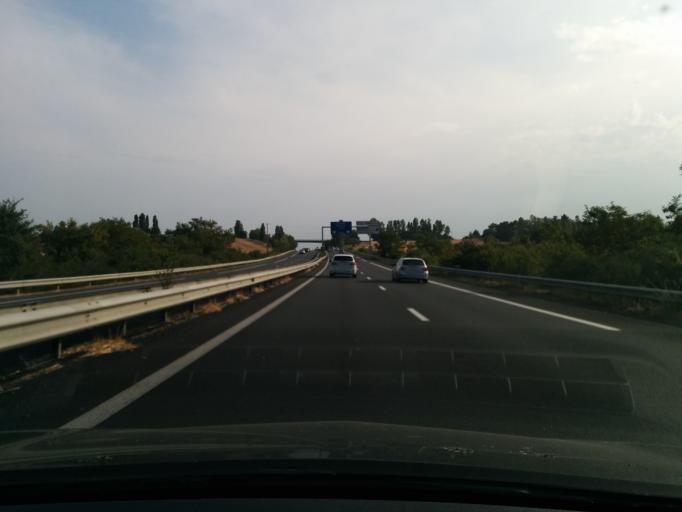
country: FR
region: Midi-Pyrenees
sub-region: Departement de la Haute-Garonne
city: Montastruc-la-Conseillere
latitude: 43.7288
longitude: 1.5741
